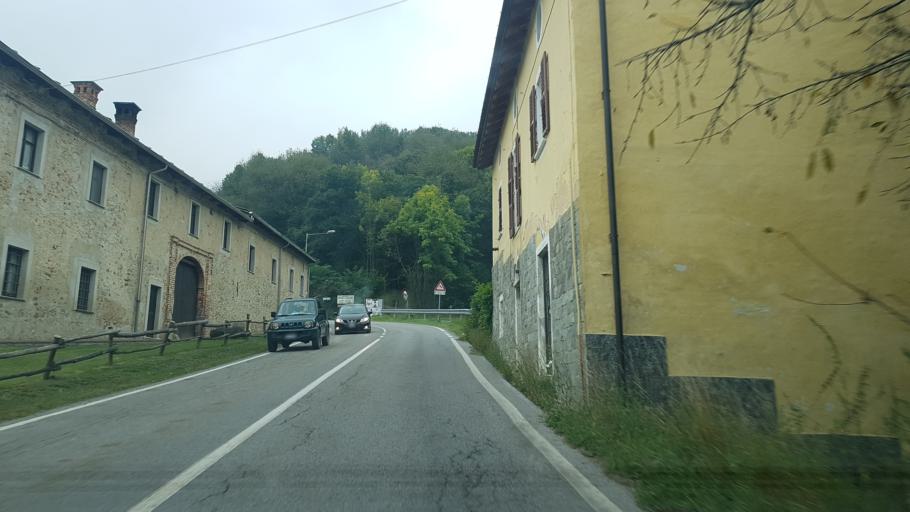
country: IT
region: Piedmont
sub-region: Provincia di Cuneo
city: Frabosa Sottana
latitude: 44.3221
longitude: 7.8007
